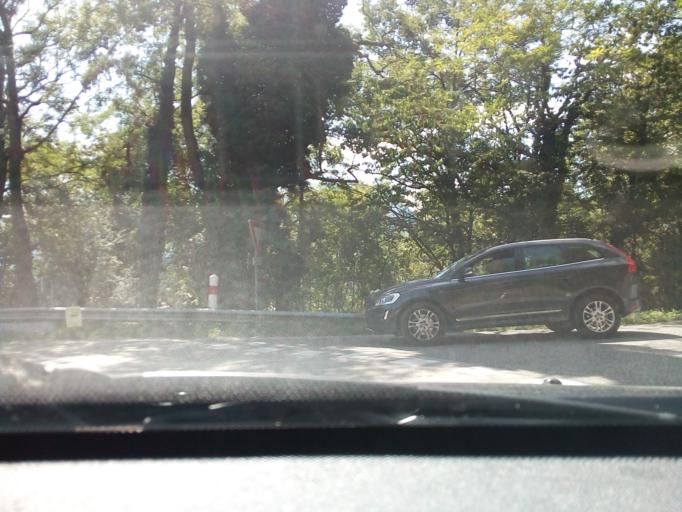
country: FR
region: Rhone-Alpes
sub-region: Departement de l'Isere
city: Vizille
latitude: 45.0918
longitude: 5.7767
